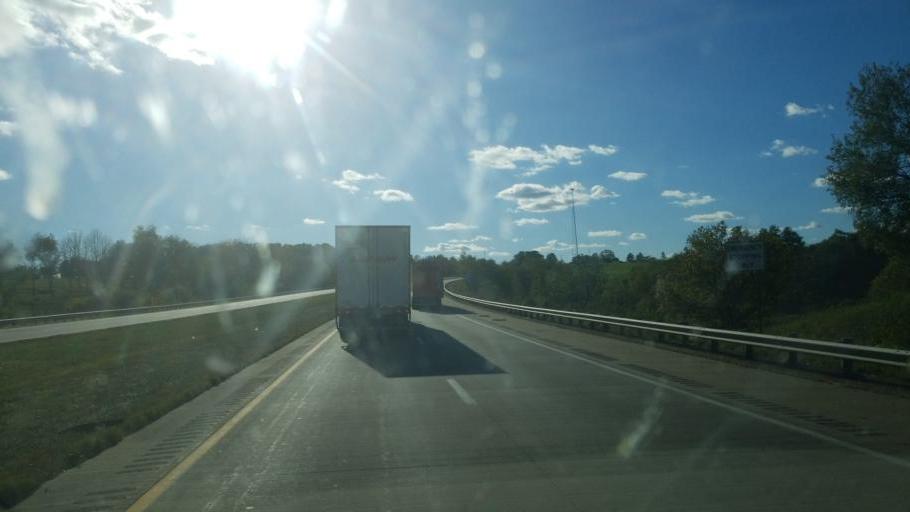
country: US
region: Ohio
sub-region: Belmont County
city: Bethesda
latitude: 40.0569
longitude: -81.0629
